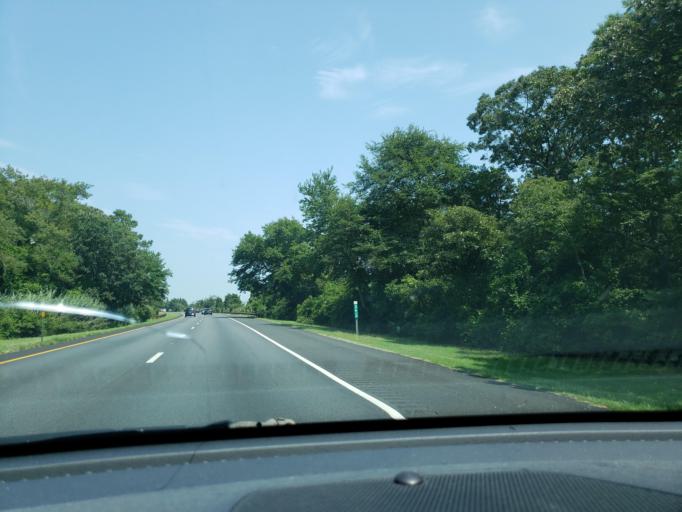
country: US
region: New Jersey
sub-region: Cape May County
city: Ocean City
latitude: 39.2717
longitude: -74.6330
